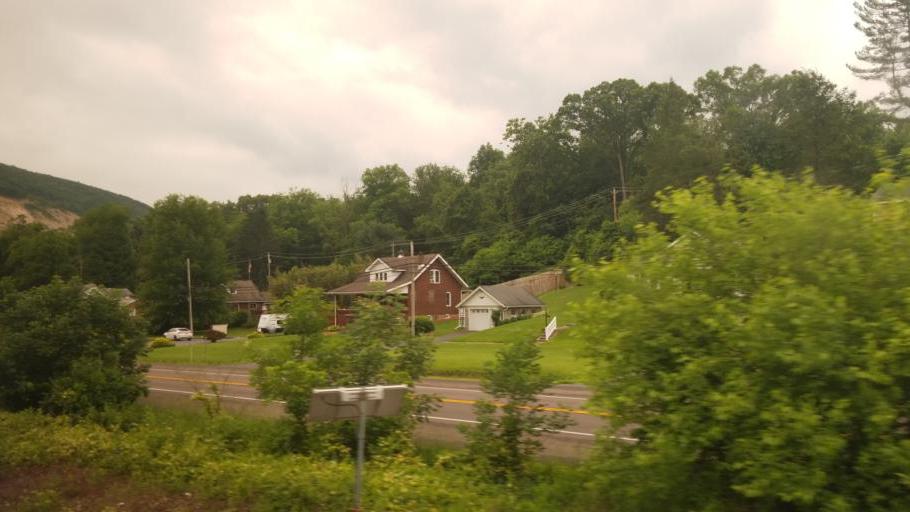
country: US
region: Maryland
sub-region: Allegany County
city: Cumberland
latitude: 39.6906
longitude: -78.7835
